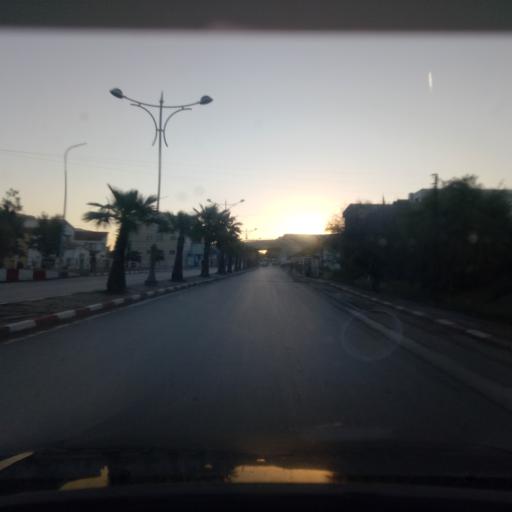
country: DZ
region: Tipaza
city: Bou Ismail
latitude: 36.6403
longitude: 2.7033
